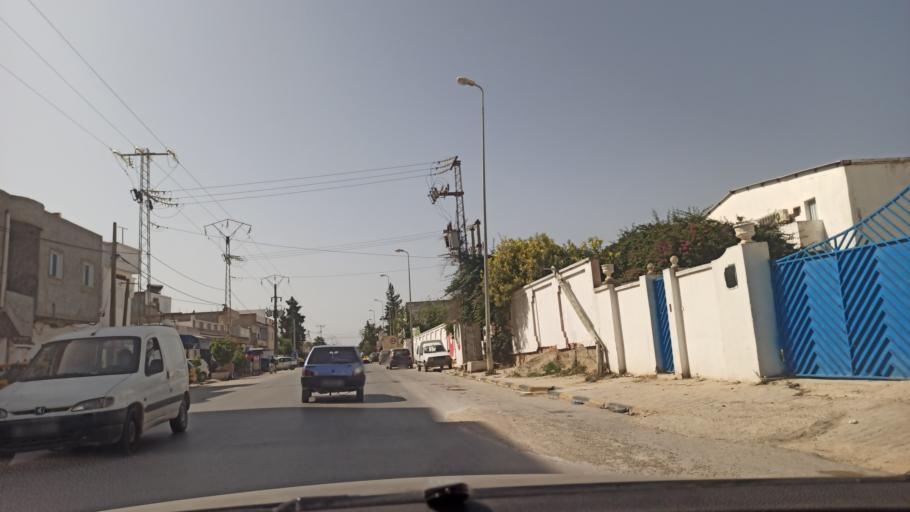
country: TN
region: Manouba
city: Manouba
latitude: 36.7615
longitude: 10.1079
